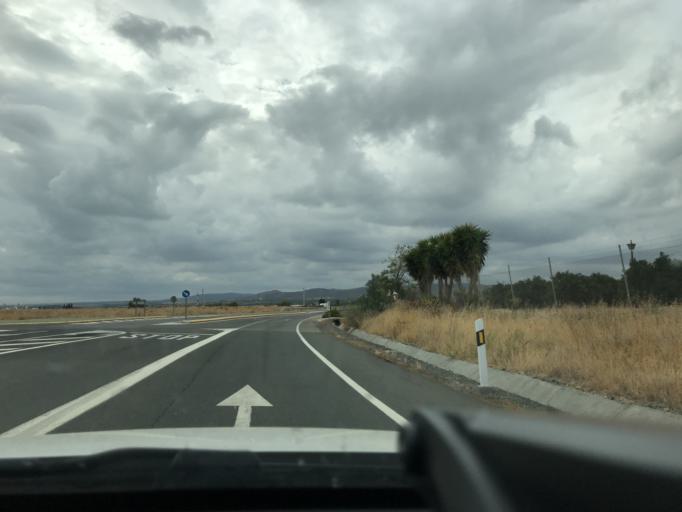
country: ES
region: Andalusia
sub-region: Provincia de Sevilla
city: Cantillana
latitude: 37.6155
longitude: -5.8079
